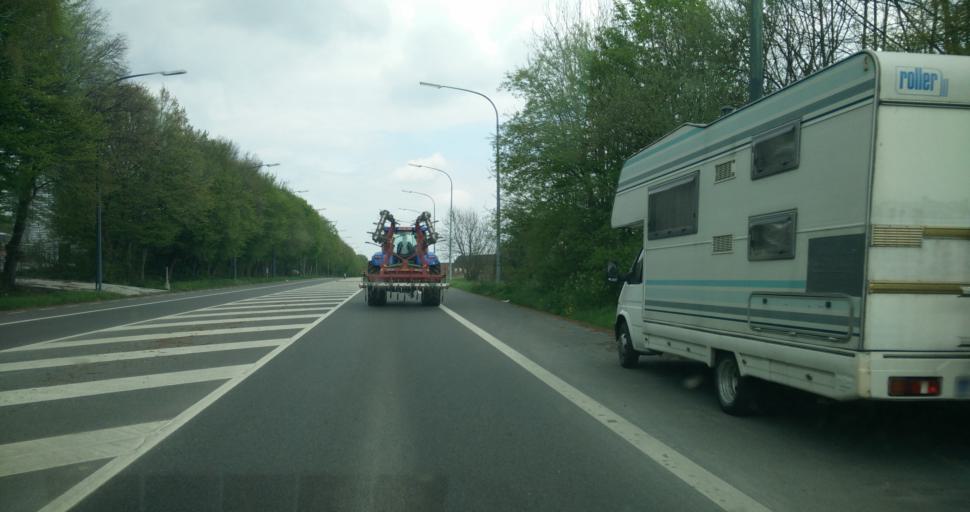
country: BE
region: Wallonia
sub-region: Province du Brabant Wallon
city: Tubize
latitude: 50.6612
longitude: 4.1715
